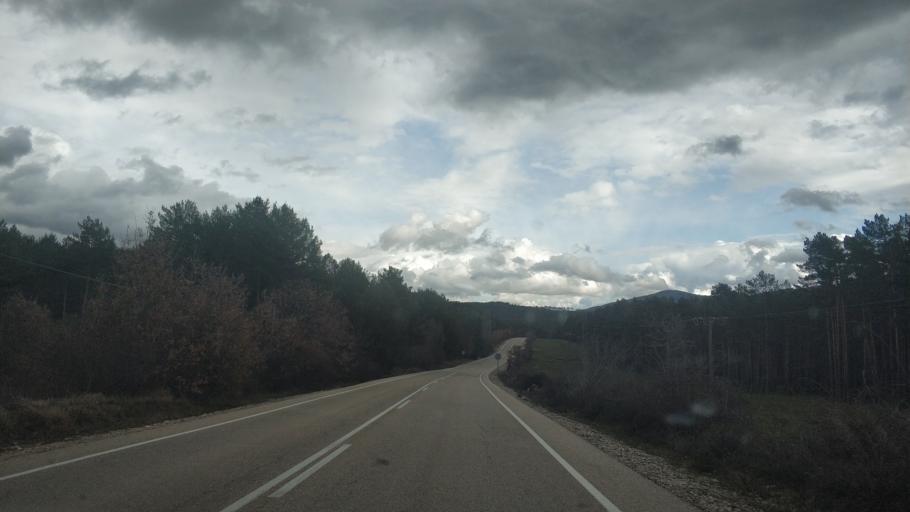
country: ES
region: Castille and Leon
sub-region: Provincia de Burgos
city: Quintanar de la Sierra
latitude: 41.9684
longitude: -3.0332
